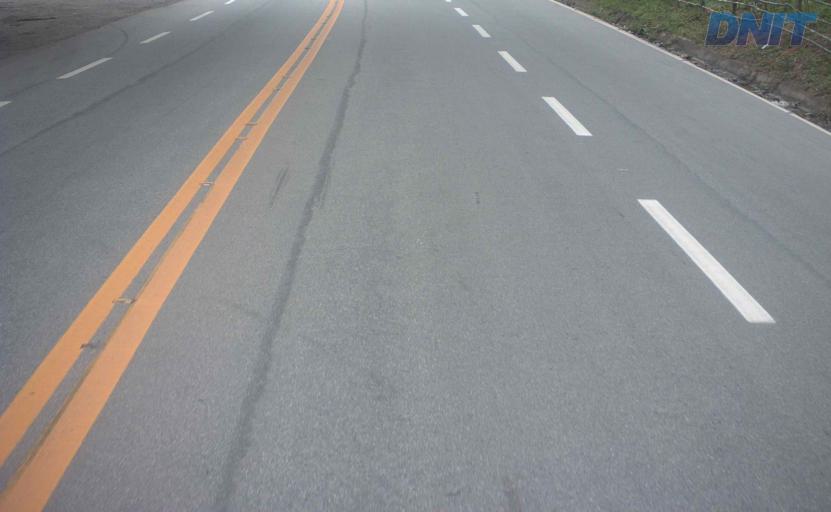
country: BR
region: Minas Gerais
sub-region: Timoteo
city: Timoteo
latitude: -19.6294
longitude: -42.8067
